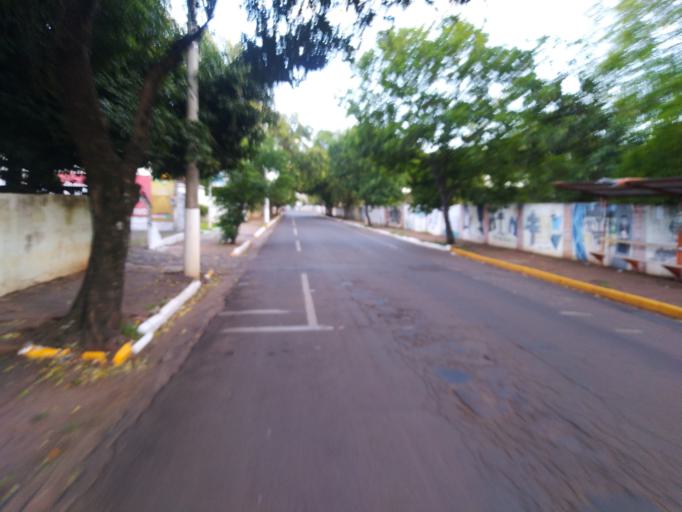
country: BR
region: Rio Grande do Sul
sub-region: Sao Borja
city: Sao Borja
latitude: -28.6536
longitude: -56.0065
